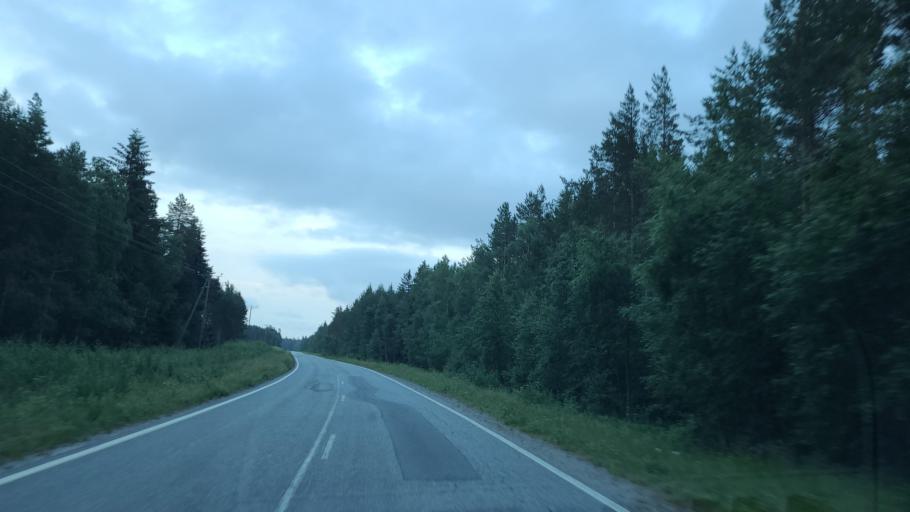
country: FI
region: Ostrobothnia
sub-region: Vaasa
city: Replot
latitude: 63.2092
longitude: 21.2559
